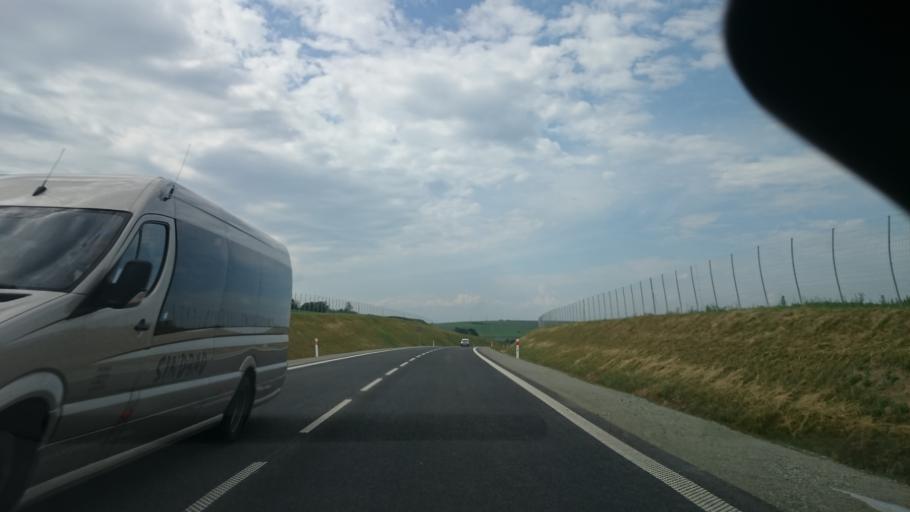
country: PL
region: Lower Silesian Voivodeship
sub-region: Powiat klodzki
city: Klodzko
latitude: 50.4092
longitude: 16.6308
